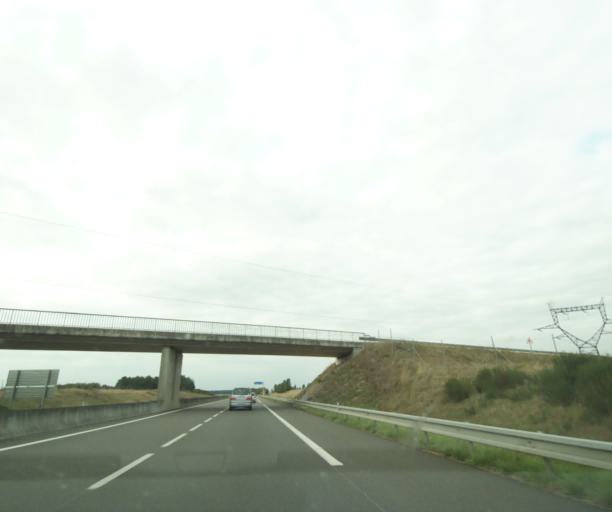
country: FR
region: Centre
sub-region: Departement d'Indre-et-Loire
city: Rouziers-de-Touraine
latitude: 47.5315
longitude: 0.6204
